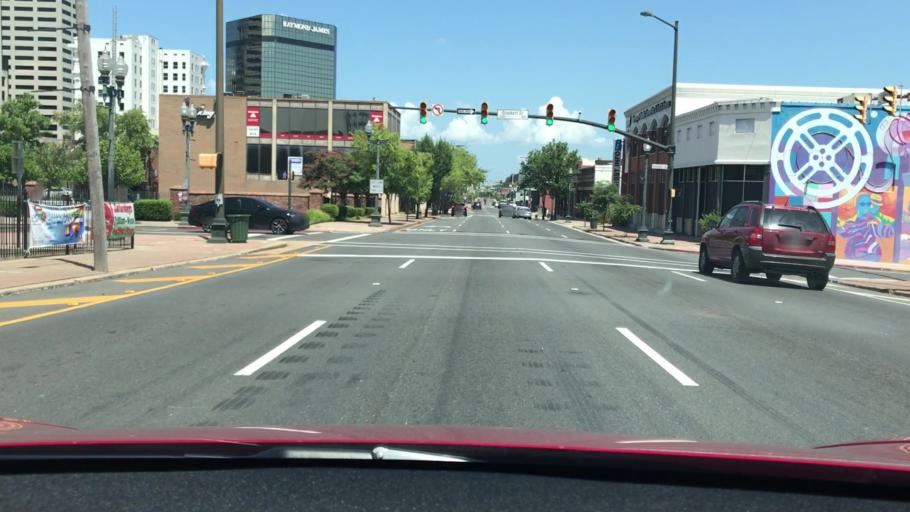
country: US
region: Louisiana
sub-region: Bossier Parish
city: Bossier City
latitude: 32.5131
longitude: -93.7449
